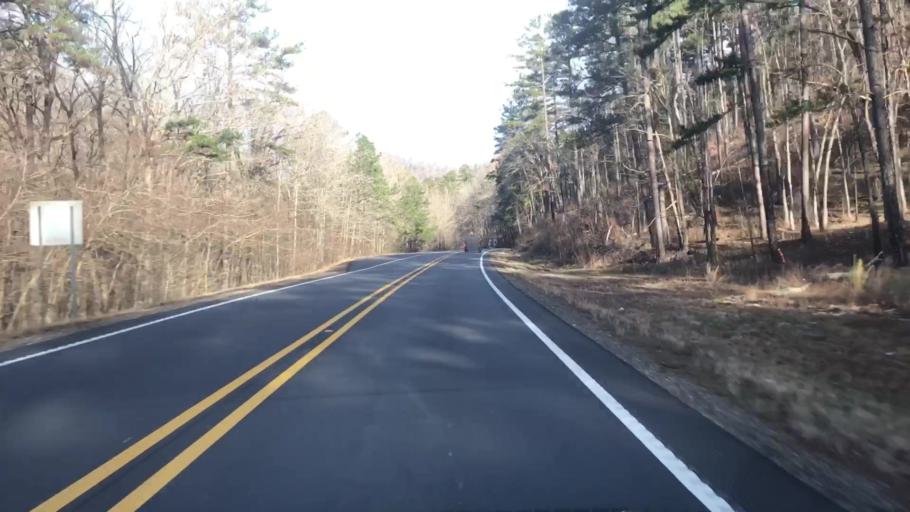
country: US
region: Arkansas
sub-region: Montgomery County
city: Mount Ida
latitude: 34.5206
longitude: -93.3896
